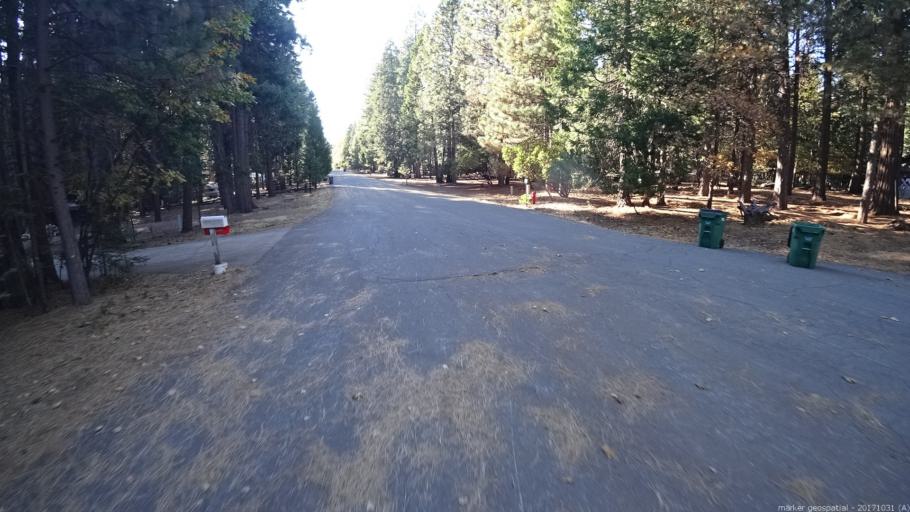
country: US
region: California
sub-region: Shasta County
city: Shingletown
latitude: 40.5037
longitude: -121.8988
